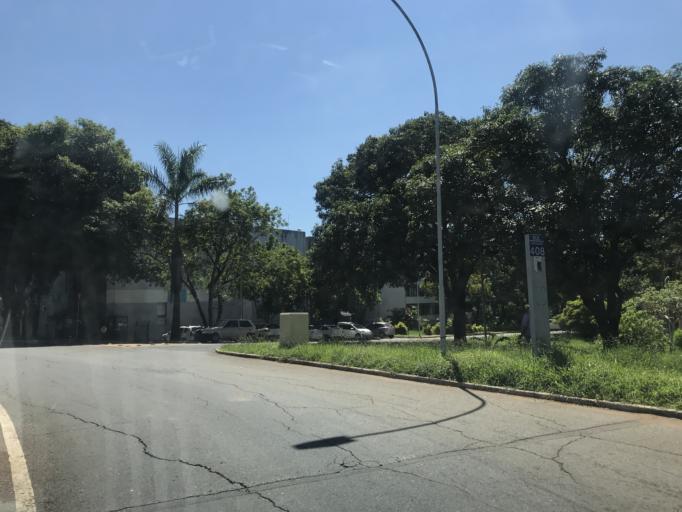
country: BR
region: Federal District
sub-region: Brasilia
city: Brasilia
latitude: -15.8203
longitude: -47.8992
